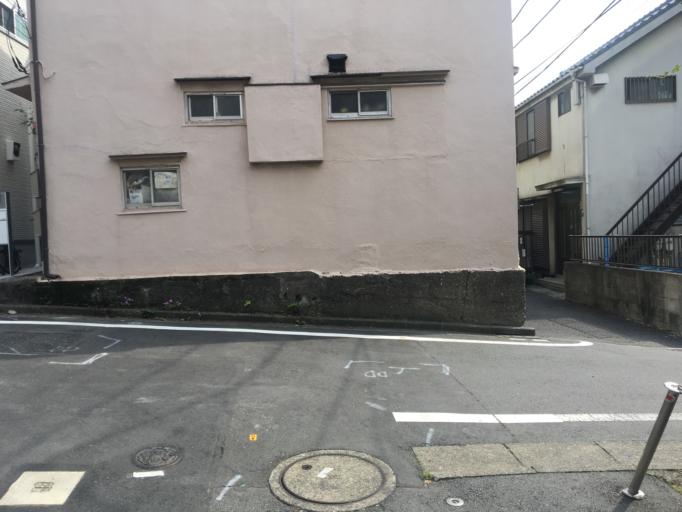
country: JP
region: Tokyo
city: Tokyo
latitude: 35.7403
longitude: 139.7163
